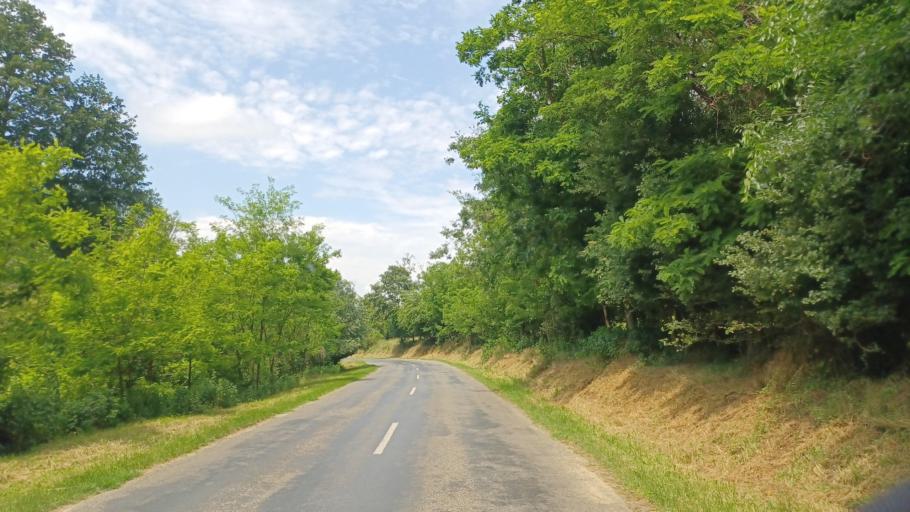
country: HU
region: Tolna
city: Simontornya
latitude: 46.7158
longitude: 18.5025
